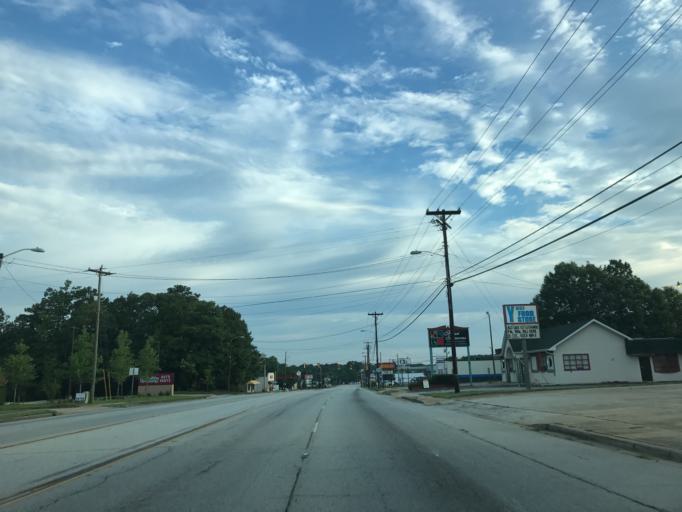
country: US
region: South Carolina
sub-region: Greenville County
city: Mauldin
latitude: 34.7812
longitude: -82.3111
